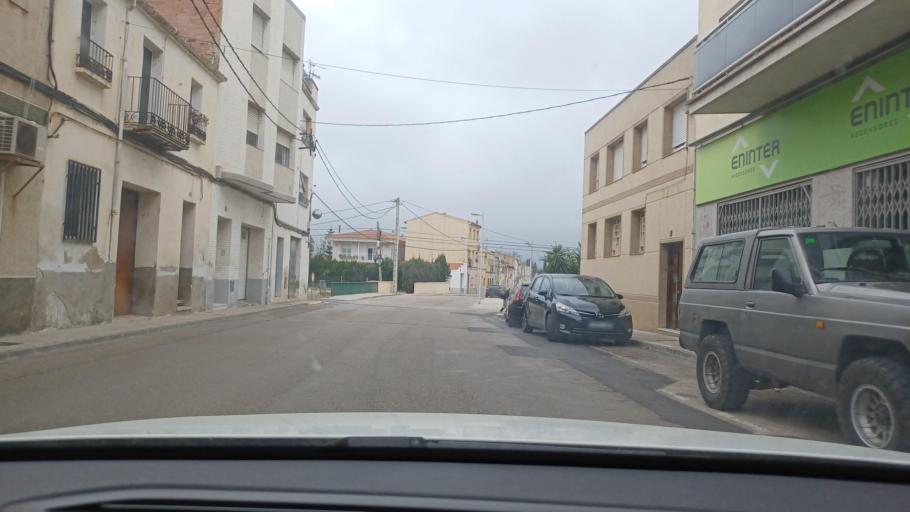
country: ES
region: Catalonia
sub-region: Provincia de Tarragona
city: Tortosa
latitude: 40.8090
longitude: 0.4975
